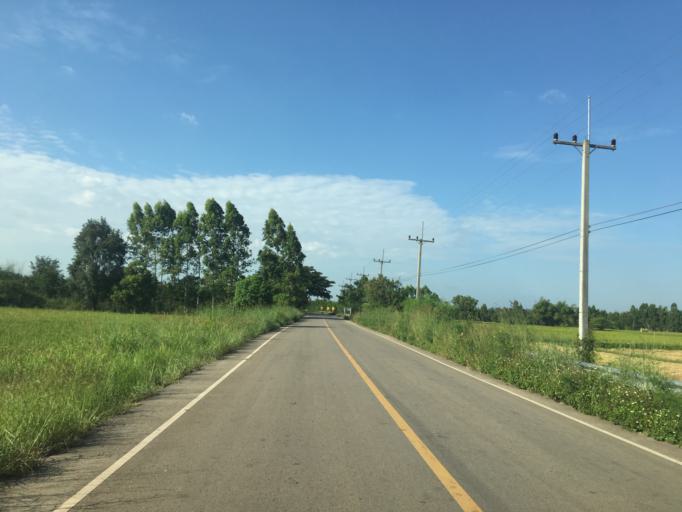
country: TH
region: Chiang Rai
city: Pa Daet
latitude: 19.4344
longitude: 100.0101
